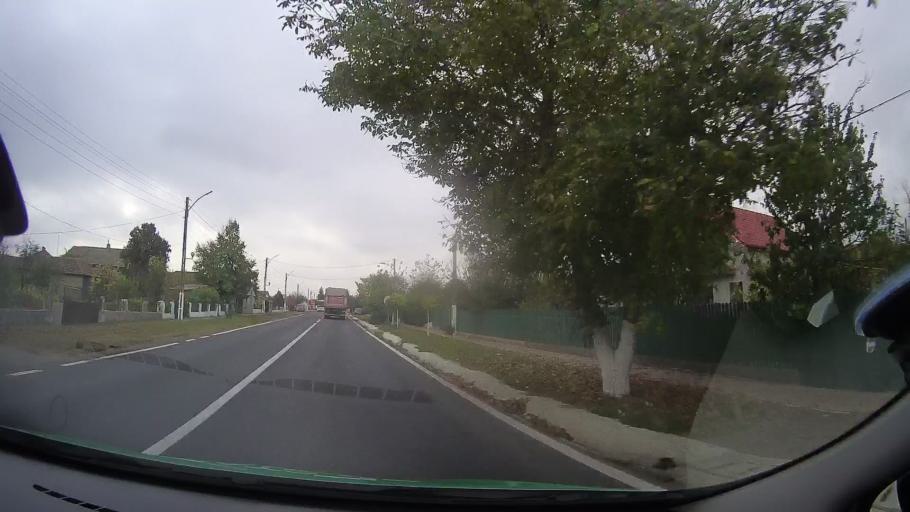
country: RO
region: Constanta
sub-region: Comuna Castelu
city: Castelu
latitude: 44.2584
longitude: 28.3433
